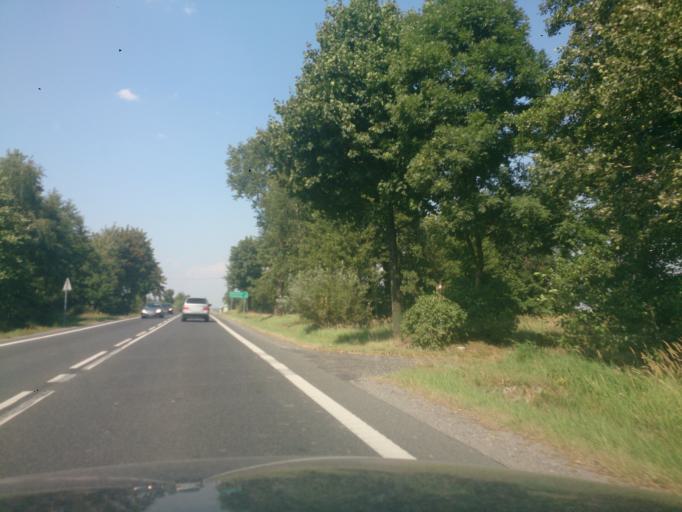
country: PL
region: Subcarpathian Voivodeship
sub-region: Powiat kolbuszowski
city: Dzikowiec
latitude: 50.2038
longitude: 21.8332
